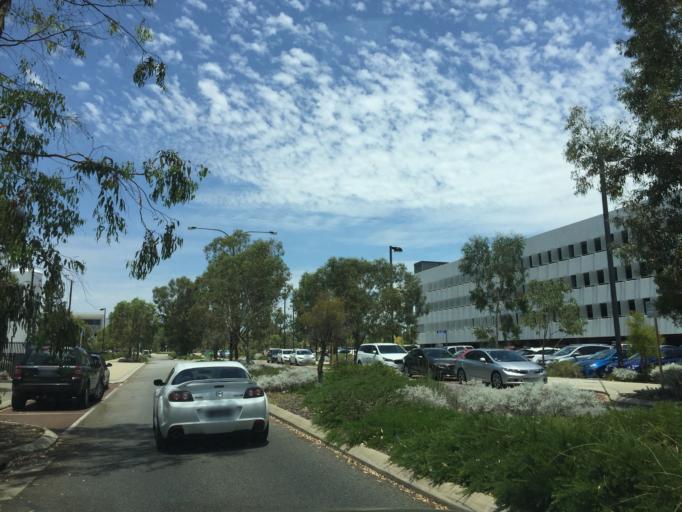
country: AU
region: Western Australia
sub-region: Melville
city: Winthrop
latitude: -32.0714
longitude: 115.8450
